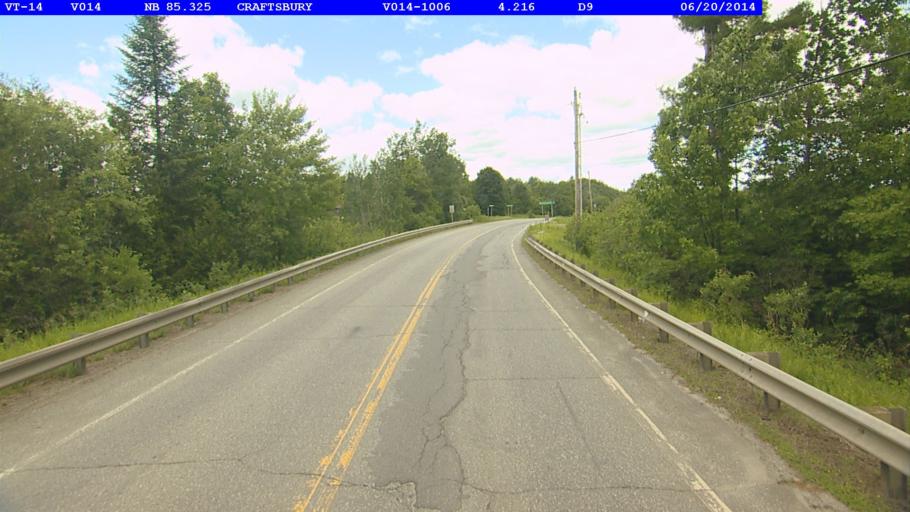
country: US
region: Vermont
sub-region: Caledonia County
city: Hardwick
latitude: 44.6515
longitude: -72.4057
